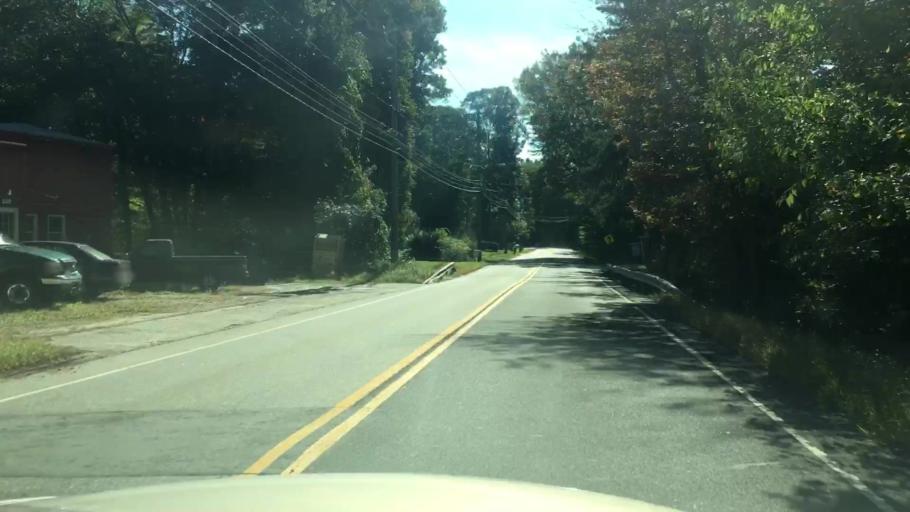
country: US
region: Connecticut
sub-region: Middlesex County
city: Westbrook Center
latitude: 41.3100
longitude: -72.4361
